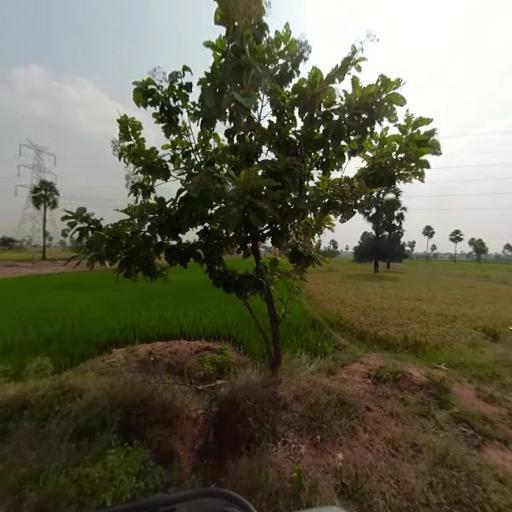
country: IN
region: Telangana
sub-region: Nalgonda
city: Suriapet
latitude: 17.2076
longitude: 79.4931
